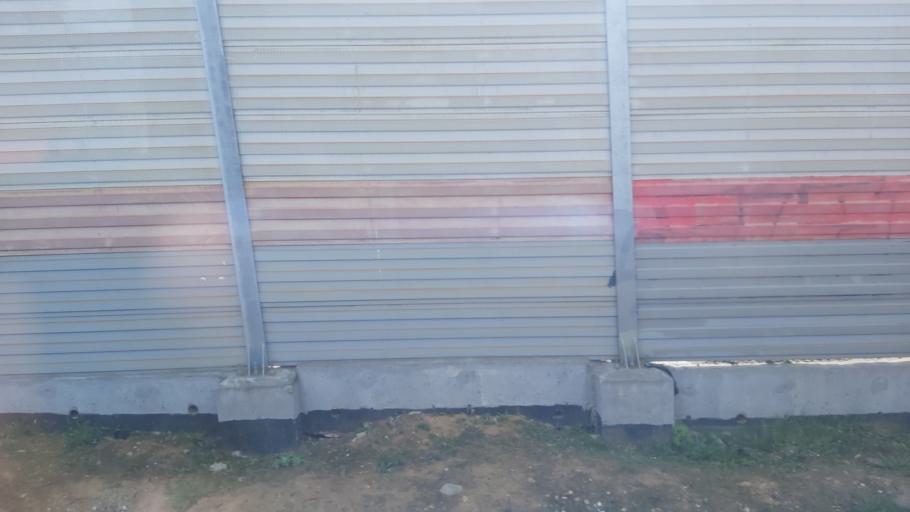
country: RU
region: Moskovskaya
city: Druzhba
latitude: 55.9008
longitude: 37.7429
